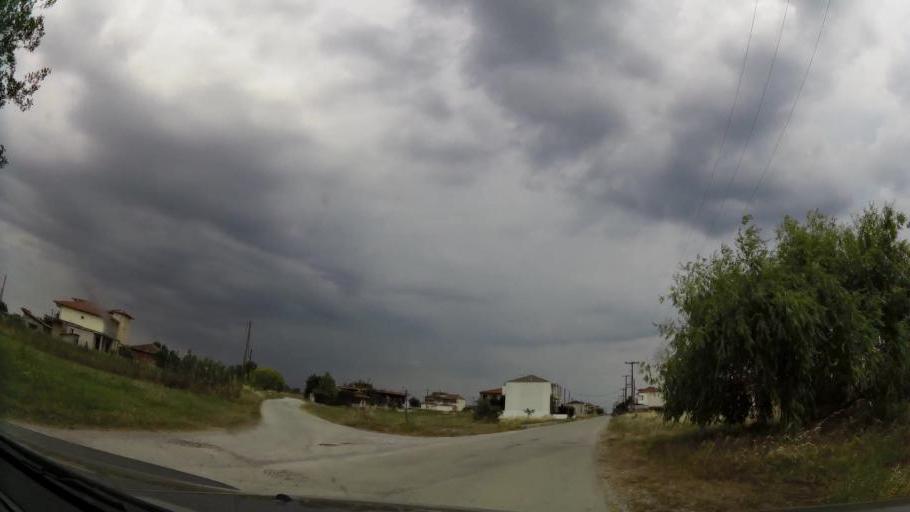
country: GR
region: Central Macedonia
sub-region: Nomos Pierias
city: Paralia
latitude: 40.2761
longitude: 22.5902
